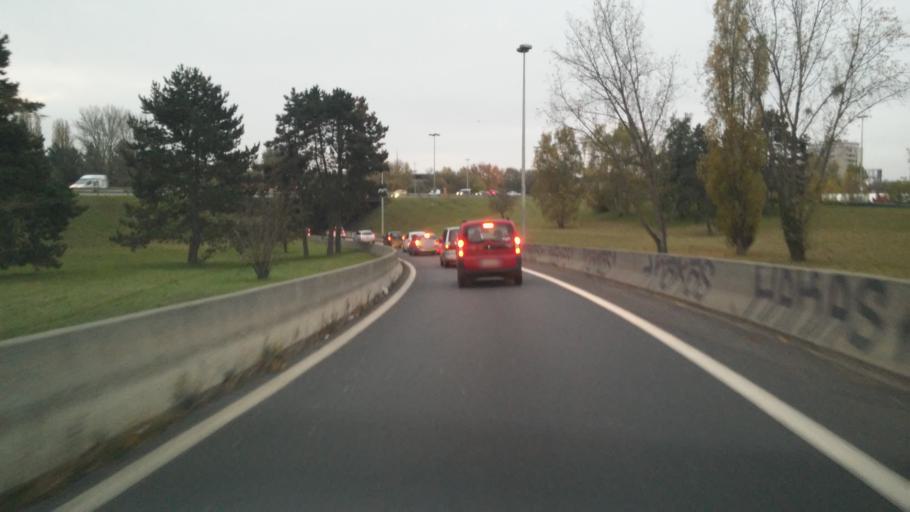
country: FR
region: Lorraine
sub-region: Departement de la Moselle
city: Le Ban Saint-Martin
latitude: 49.1156
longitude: 6.1599
